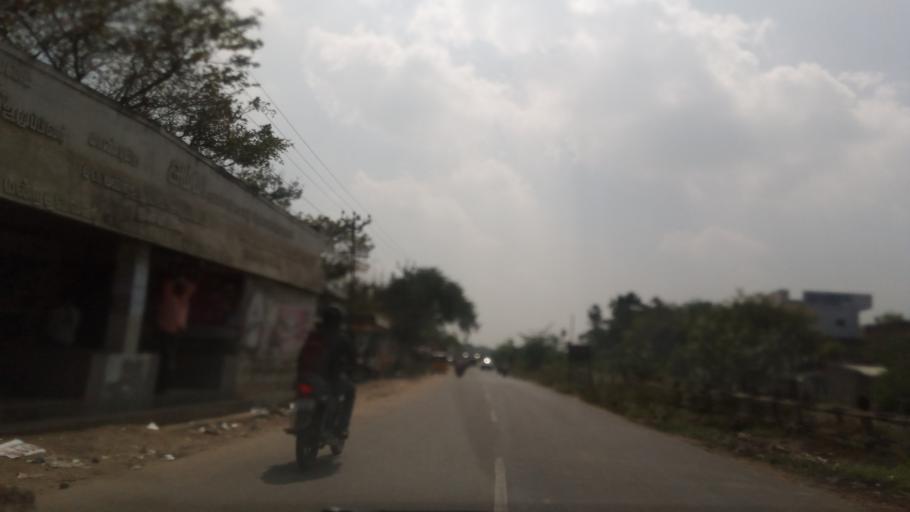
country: IN
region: Tamil Nadu
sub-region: Vellore
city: Arakkonam
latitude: 13.0748
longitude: 79.6710
